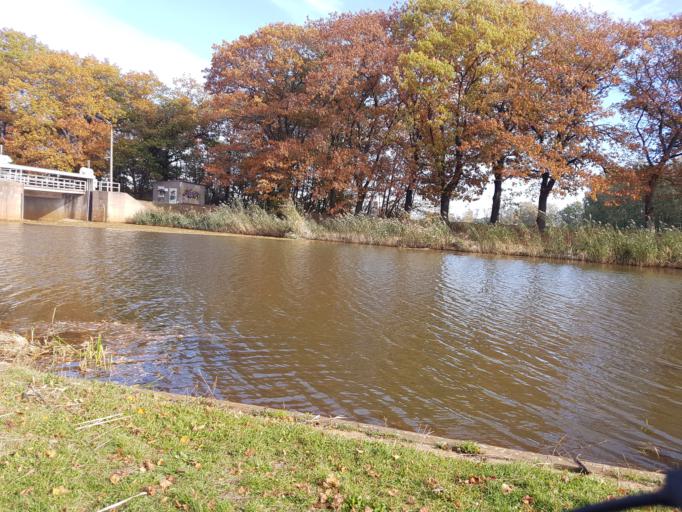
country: DE
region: Brandenburg
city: Schilda
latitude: 51.5981
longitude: 13.3234
